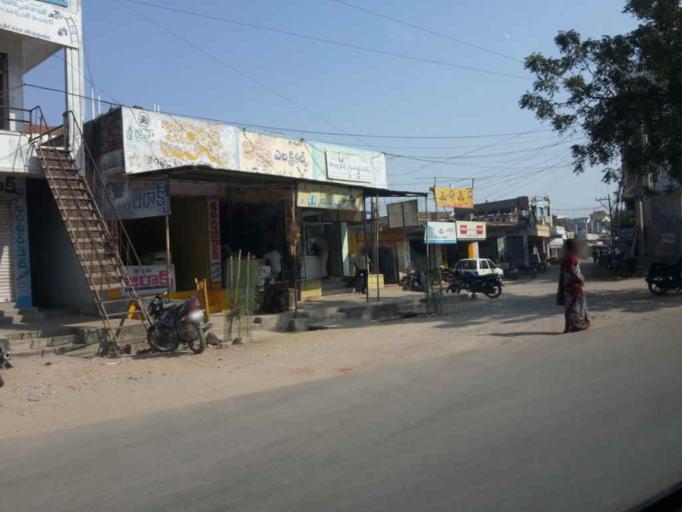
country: IN
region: Telangana
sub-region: Karimnagar
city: Koratla
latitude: 18.8489
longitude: 78.6204
